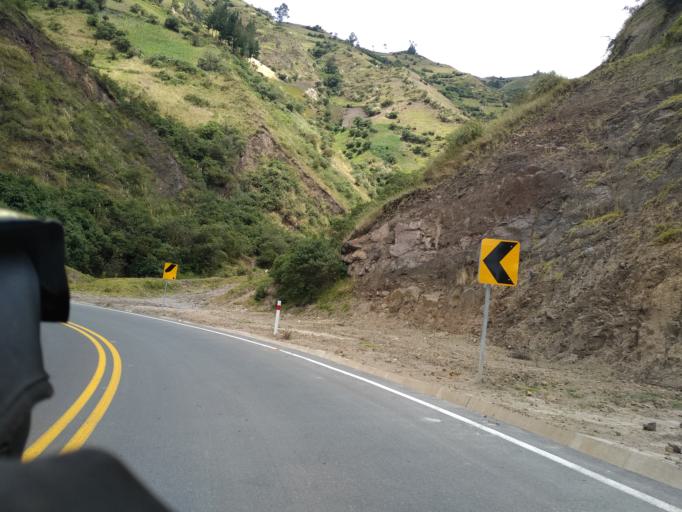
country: EC
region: Cotopaxi
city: Saquisili
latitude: -0.7653
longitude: -78.9139
